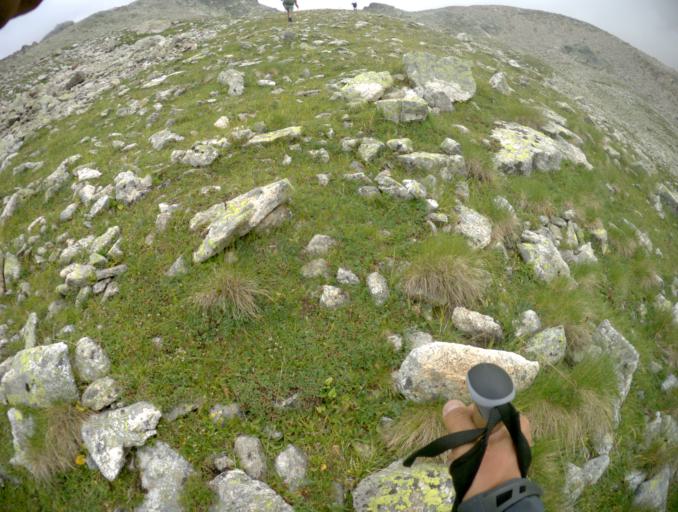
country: RU
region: Karachayevo-Cherkesiya
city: Uchkulan
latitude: 43.2835
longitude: 42.0997
